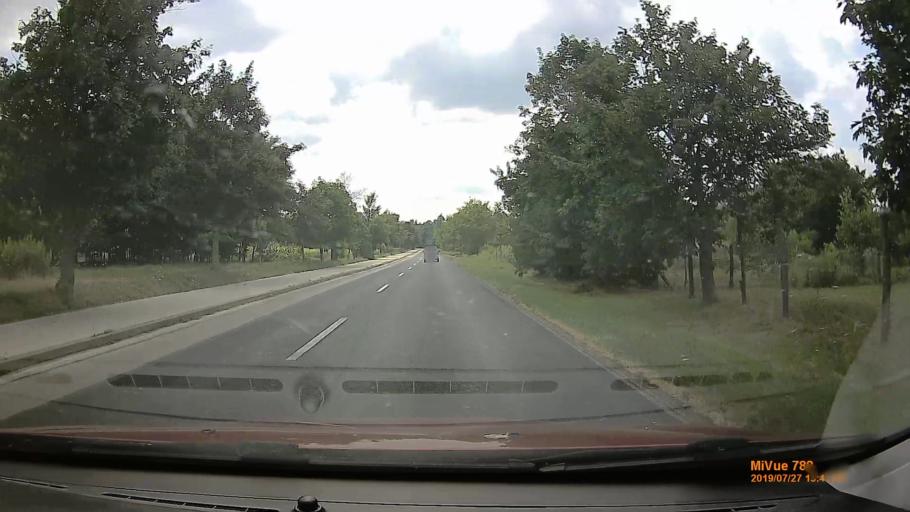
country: HU
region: Veszprem
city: Ajka
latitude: 47.1269
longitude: 17.5680
